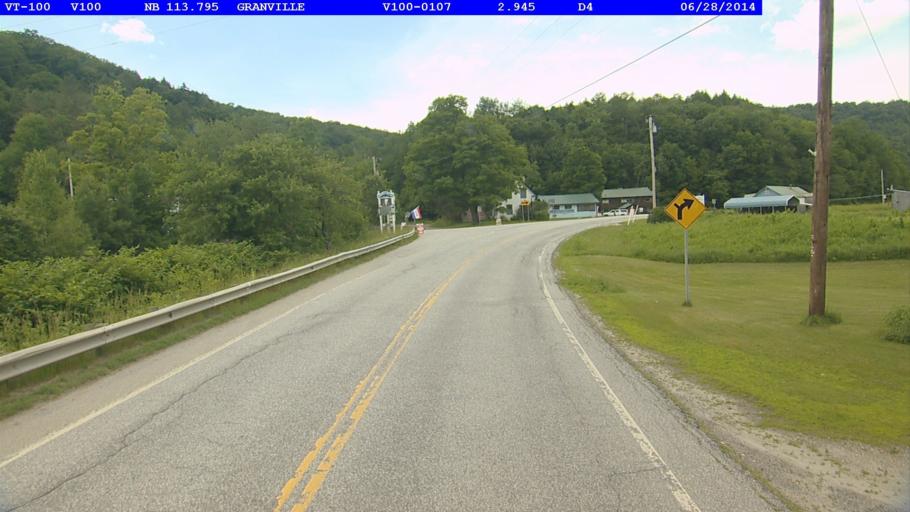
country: US
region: Vermont
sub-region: Orange County
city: Randolph
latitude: 43.9851
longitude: -72.8474
